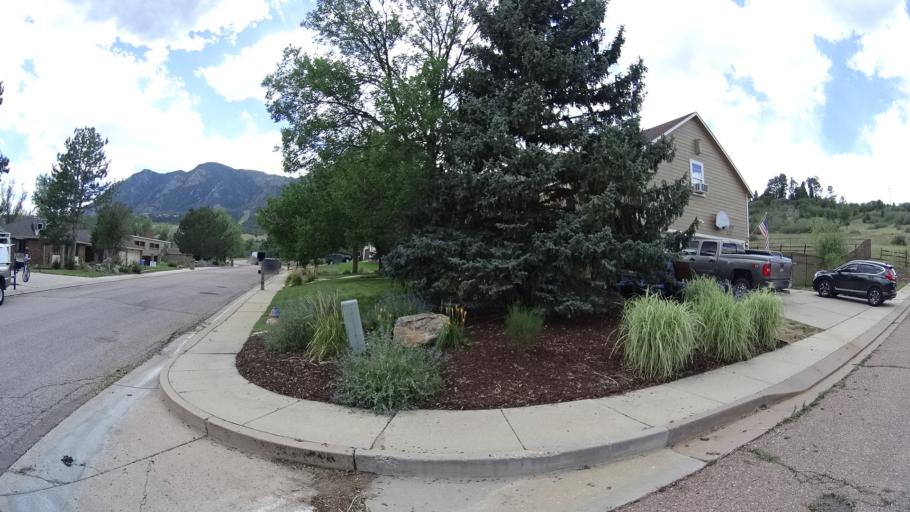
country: US
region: Colorado
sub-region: El Paso County
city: Stratmoor
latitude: 38.7799
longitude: -104.8327
